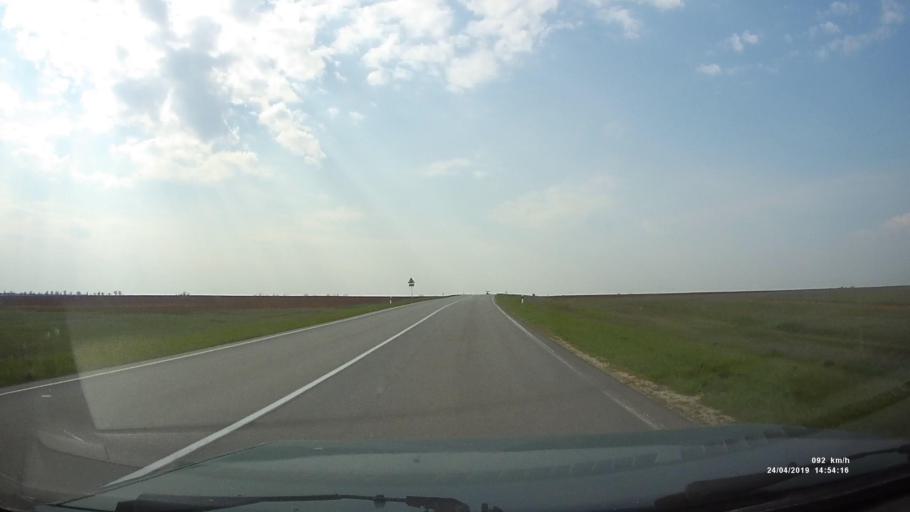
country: RU
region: Rostov
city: Remontnoye
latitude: 46.5333
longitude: 43.6418
